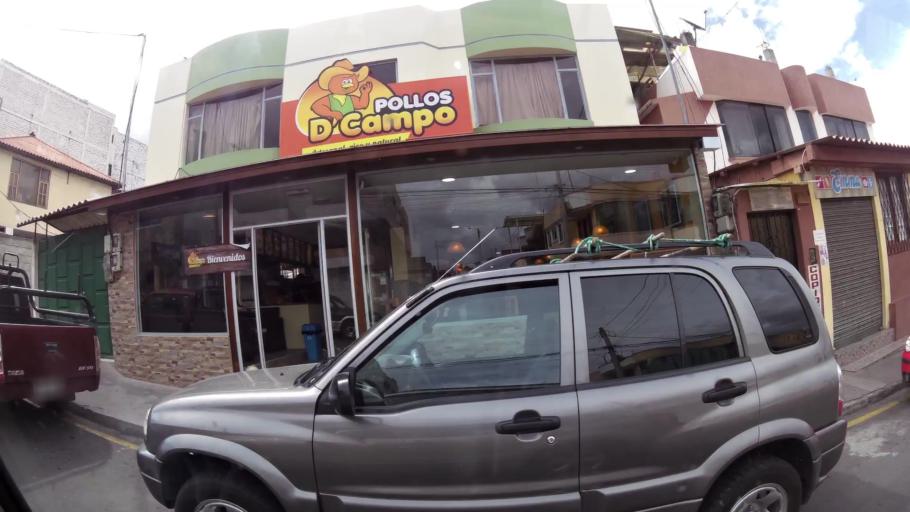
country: EC
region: Tungurahua
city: Ambato
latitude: -1.2563
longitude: -78.6336
